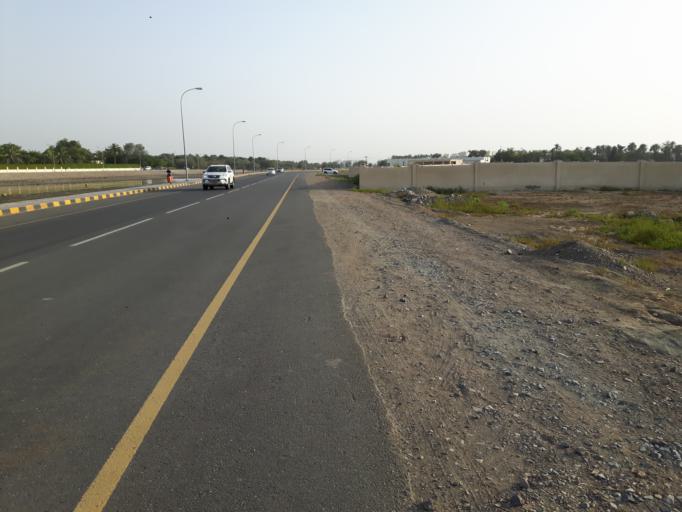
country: OM
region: Al Batinah
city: Al Sohar
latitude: 24.4048
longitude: 56.7121
